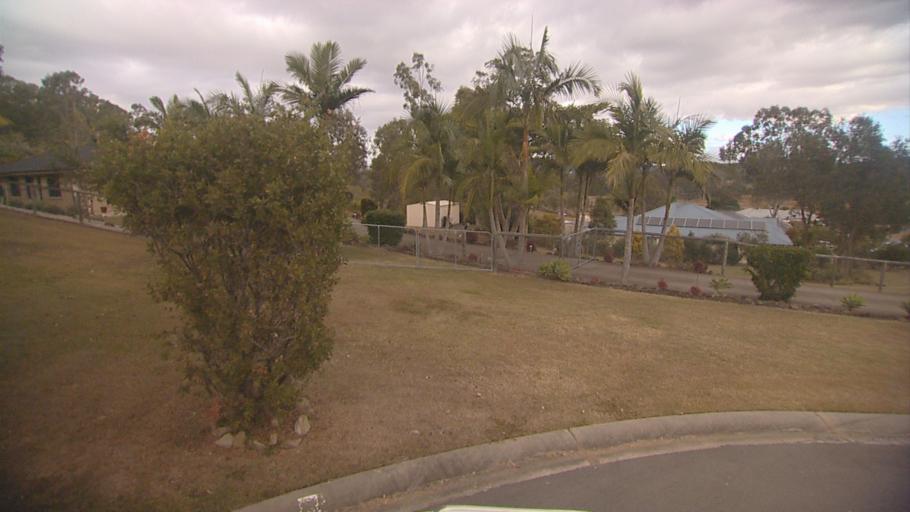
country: AU
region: Queensland
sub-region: Logan
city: Cedar Vale
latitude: -27.8777
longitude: 153.0760
